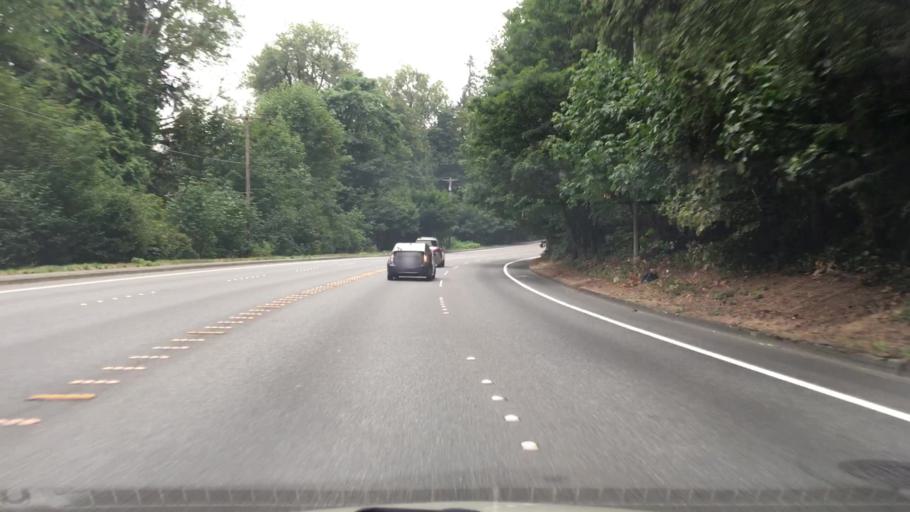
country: US
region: Washington
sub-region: King County
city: Newcastle
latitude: 47.5504
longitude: -122.1666
